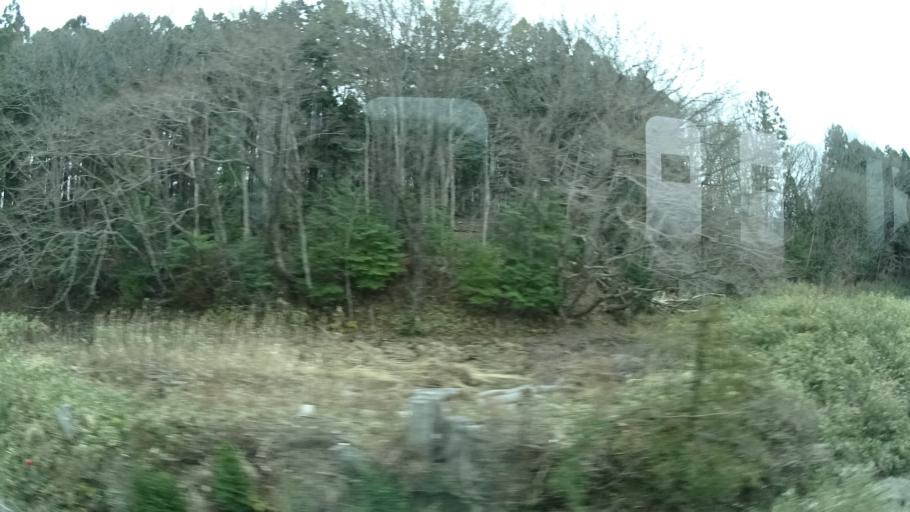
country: JP
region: Fukushima
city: Namie
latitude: 37.3514
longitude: 140.9942
